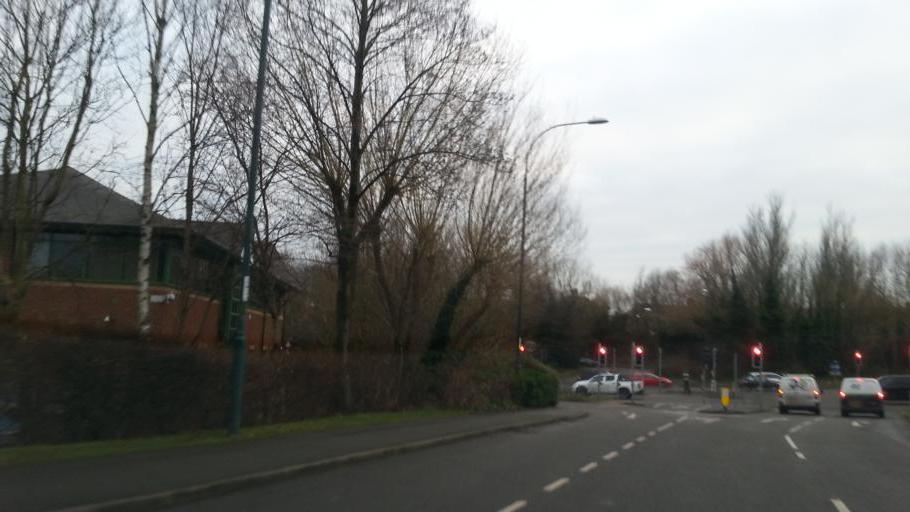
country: GB
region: England
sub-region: Nottinghamshire
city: Hucknall
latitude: 52.9878
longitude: -1.2071
